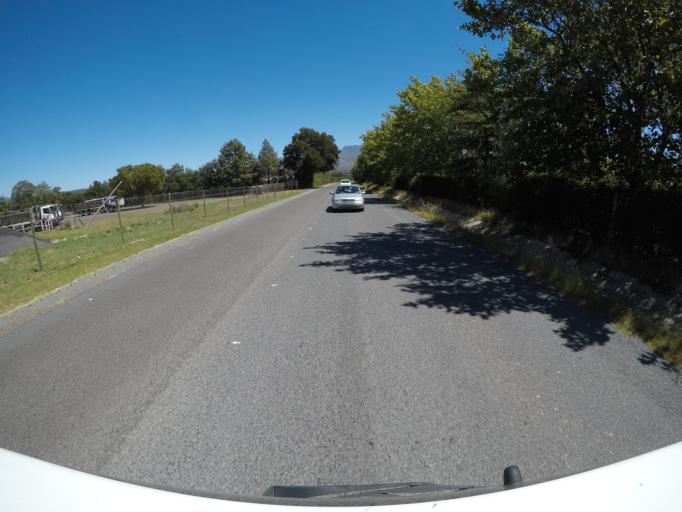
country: ZA
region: Western Cape
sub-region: Overberg District Municipality
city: Grabouw
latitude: -34.1787
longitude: 19.0359
